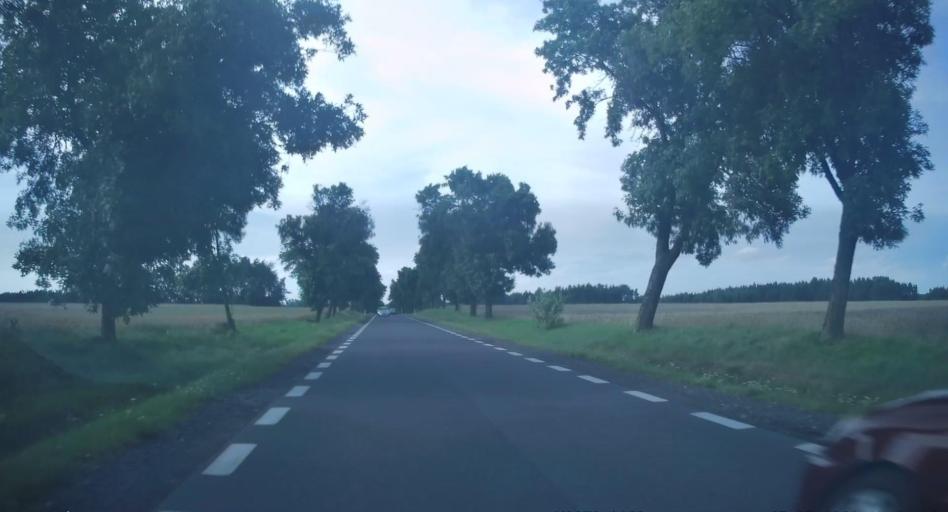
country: PL
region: Lodz Voivodeship
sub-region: Powiat tomaszowski
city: Rzeczyca
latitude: 51.6336
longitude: 20.2901
